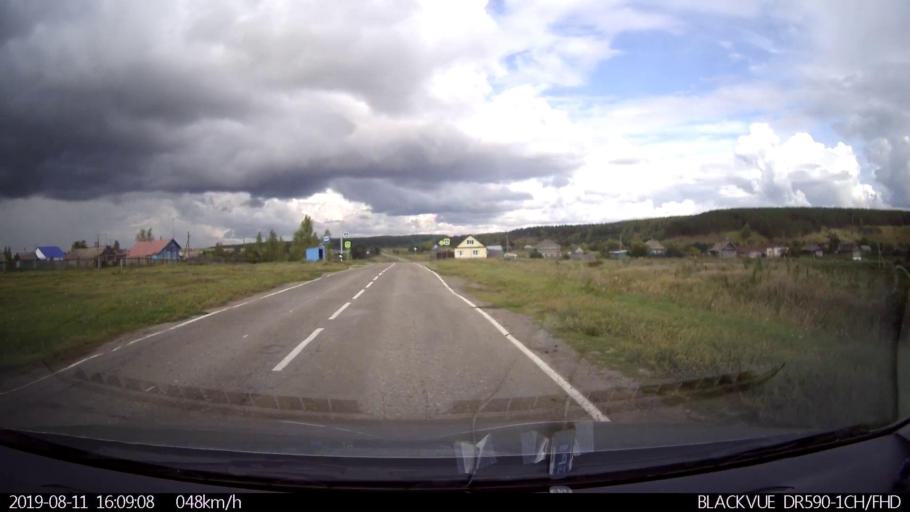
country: RU
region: Ulyanovsk
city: Ignatovka
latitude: 53.9899
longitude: 47.6509
